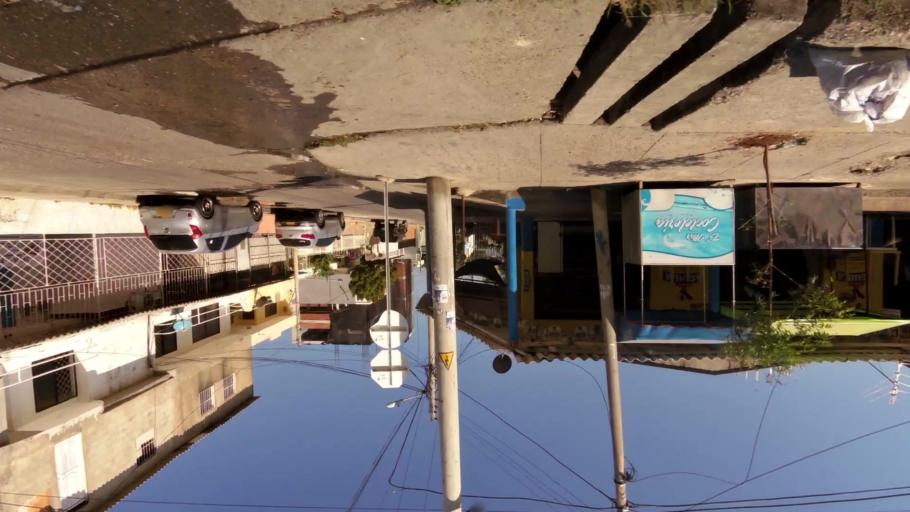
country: CO
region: Bolivar
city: Cartagena
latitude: 10.3908
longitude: -75.5036
